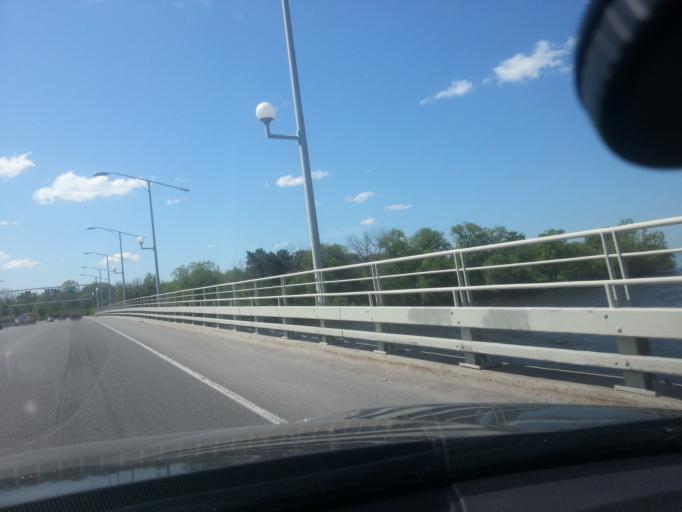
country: CA
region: Ontario
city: Ottawa
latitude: 45.4058
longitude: -75.7552
